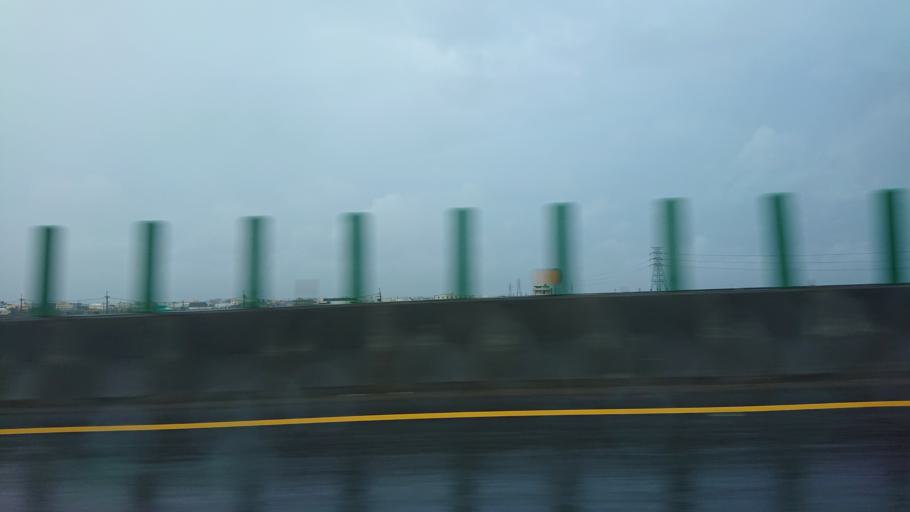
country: TW
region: Taiwan
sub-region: Changhua
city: Chang-hua
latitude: 24.1274
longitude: 120.4393
